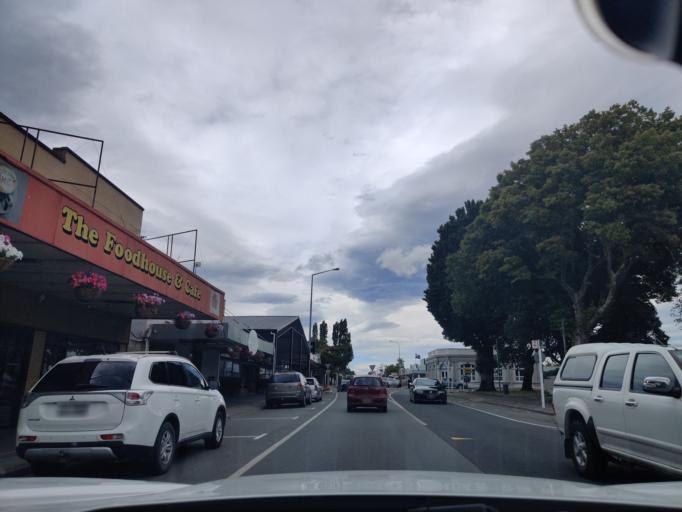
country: NZ
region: Wellington
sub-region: Masterton District
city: Masterton
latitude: -41.0237
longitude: 175.5286
